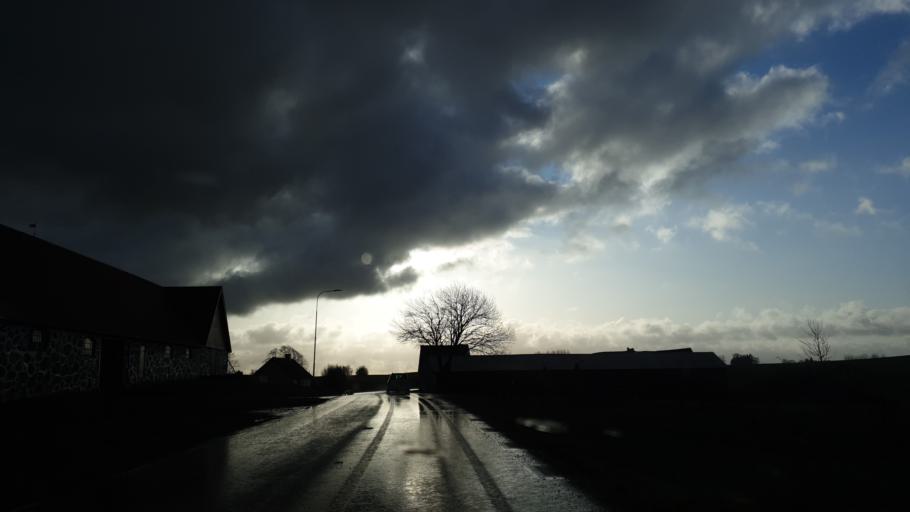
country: SE
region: Skane
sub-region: Skurups Kommun
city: Rydsgard
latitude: 55.4664
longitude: 13.5641
